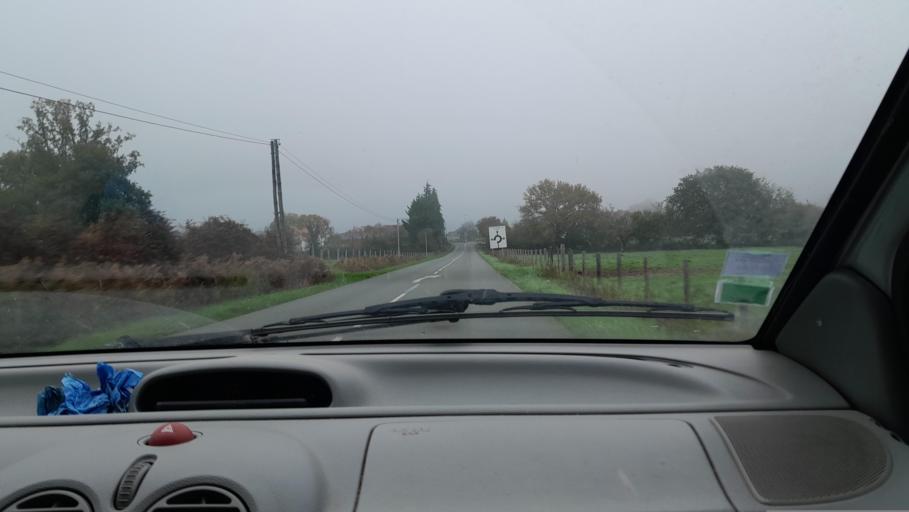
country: FR
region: Pays de la Loire
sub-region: Departement de la Mayenne
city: Saint-Berthevin
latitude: 48.0599
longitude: -0.8465
